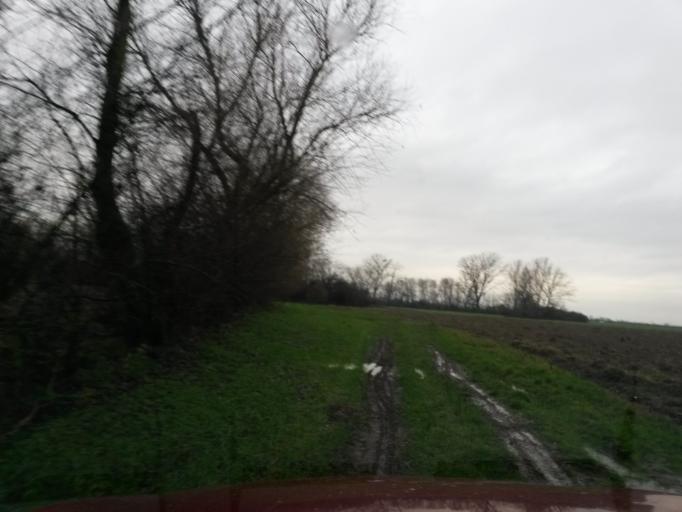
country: SK
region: Kosicky
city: Sobrance
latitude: 48.6421
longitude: 22.0809
